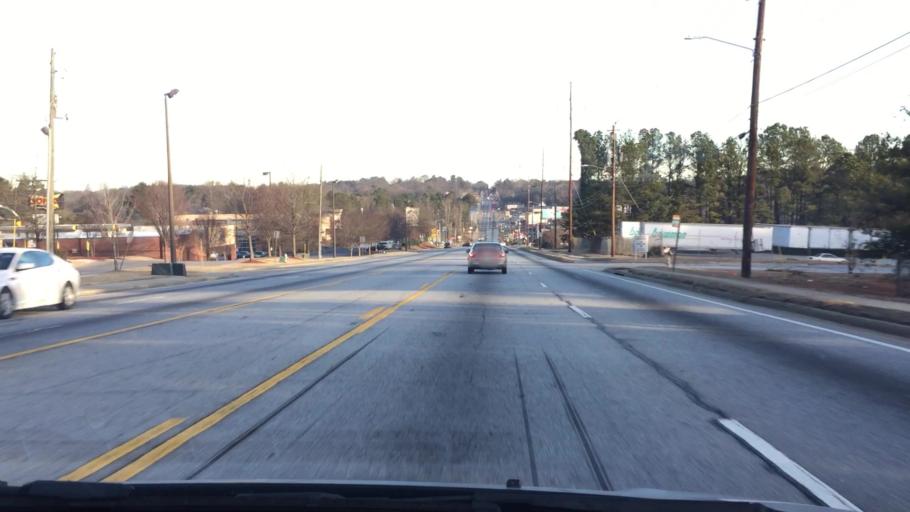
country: US
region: Georgia
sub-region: DeKalb County
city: Gresham Park
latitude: 33.7126
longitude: -84.3495
